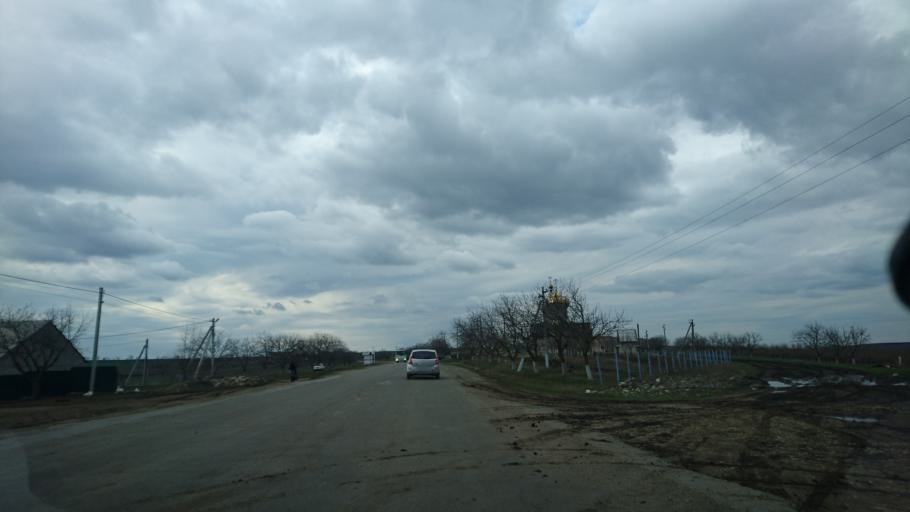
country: MD
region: Gagauzia
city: Comrat
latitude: 46.3058
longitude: 28.6236
